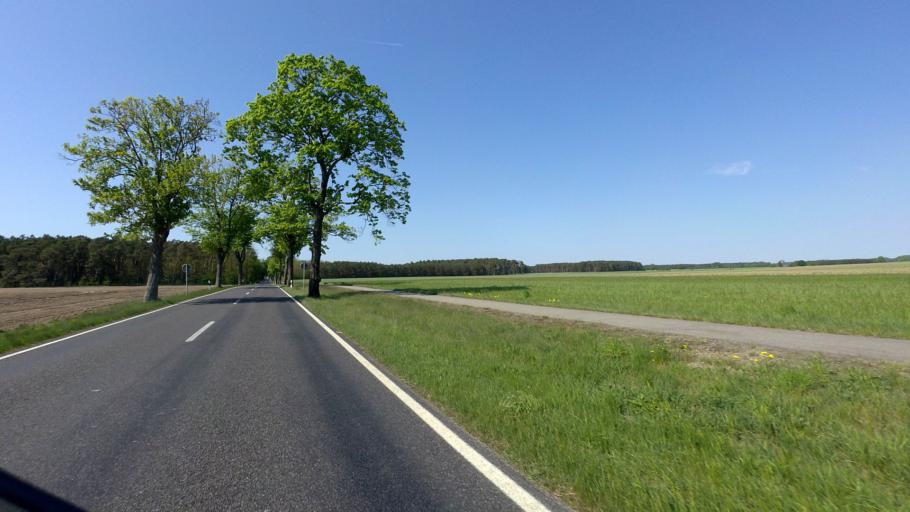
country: DE
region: Brandenburg
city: Neu Zauche
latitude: 52.0086
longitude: 14.0509
